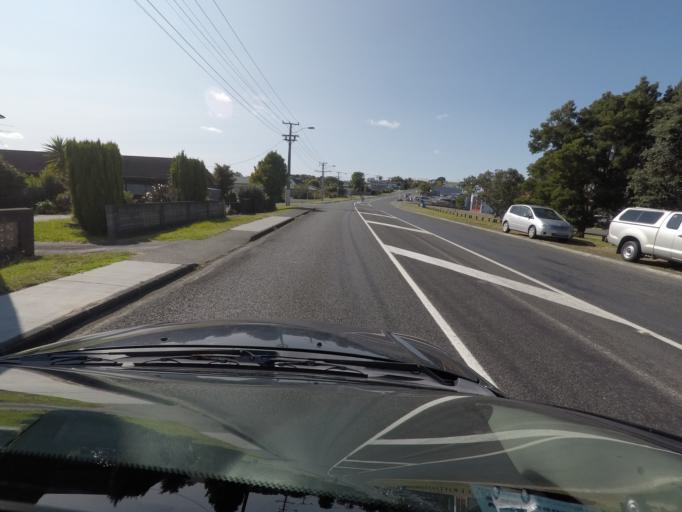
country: NZ
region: Auckland
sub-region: Auckland
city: Warkworth
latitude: -36.4226
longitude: 174.7261
